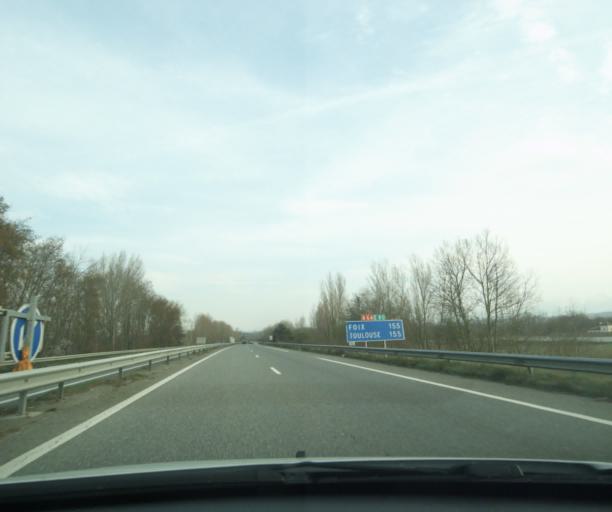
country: FR
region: Midi-Pyrenees
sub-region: Departement des Hautes-Pyrenees
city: Juillan
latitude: 43.2148
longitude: 0.0301
